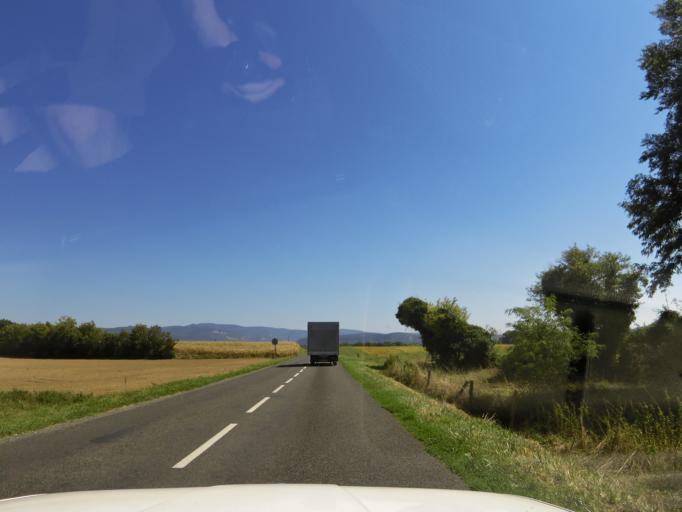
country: FR
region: Rhone-Alpes
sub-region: Departement de l'Ain
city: Chazey-sur-Ain
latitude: 45.8918
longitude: 5.2587
